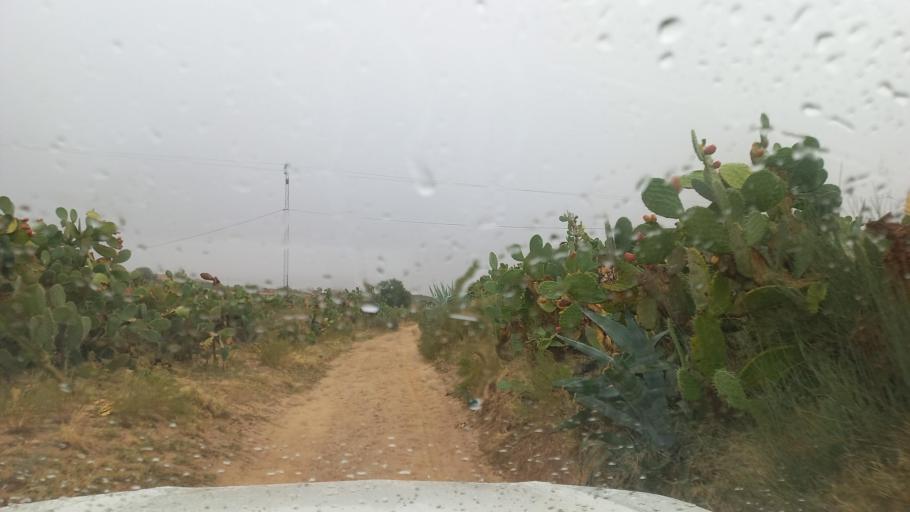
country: TN
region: Al Qasrayn
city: Kasserine
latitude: 35.2726
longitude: 8.9432
